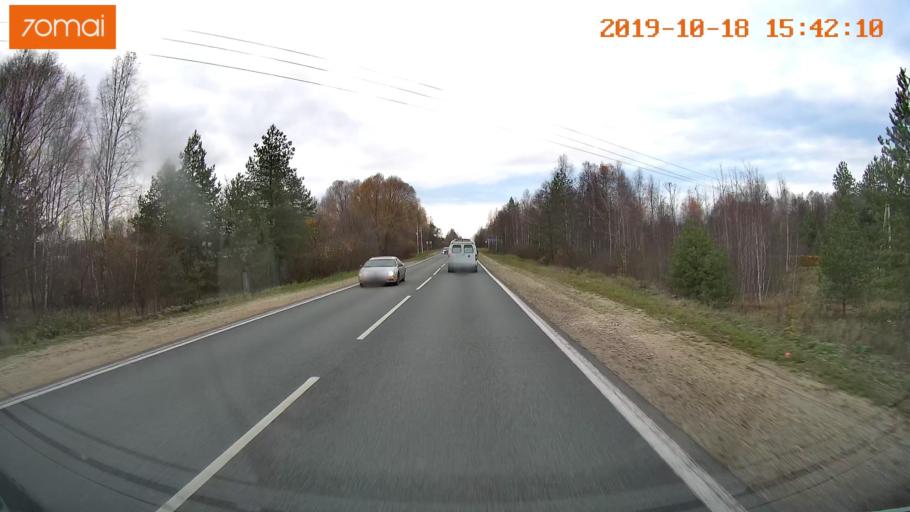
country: RU
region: Vladimir
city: Golovino
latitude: 55.9528
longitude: 40.5719
